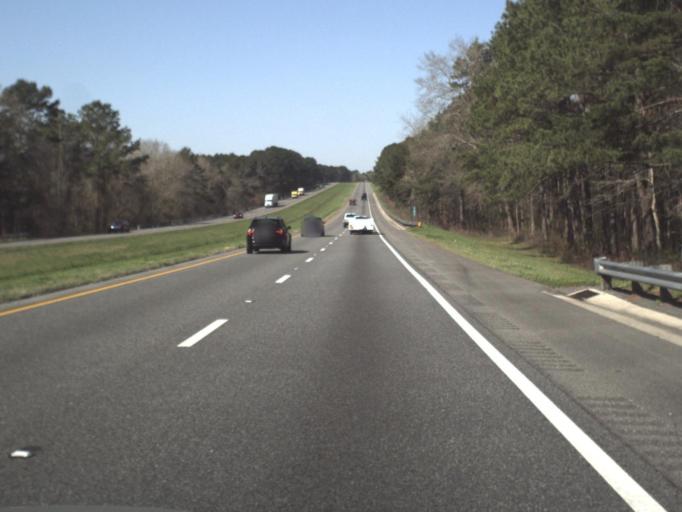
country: US
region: Florida
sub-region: Gadsden County
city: Quincy
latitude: 30.5308
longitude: -84.5552
